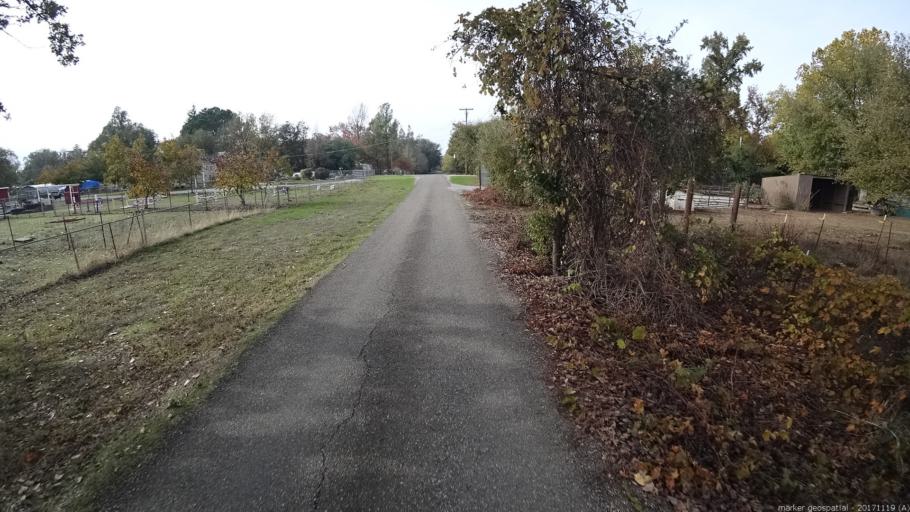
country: US
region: California
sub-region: Shasta County
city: Anderson
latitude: 40.4869
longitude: -122.2865
